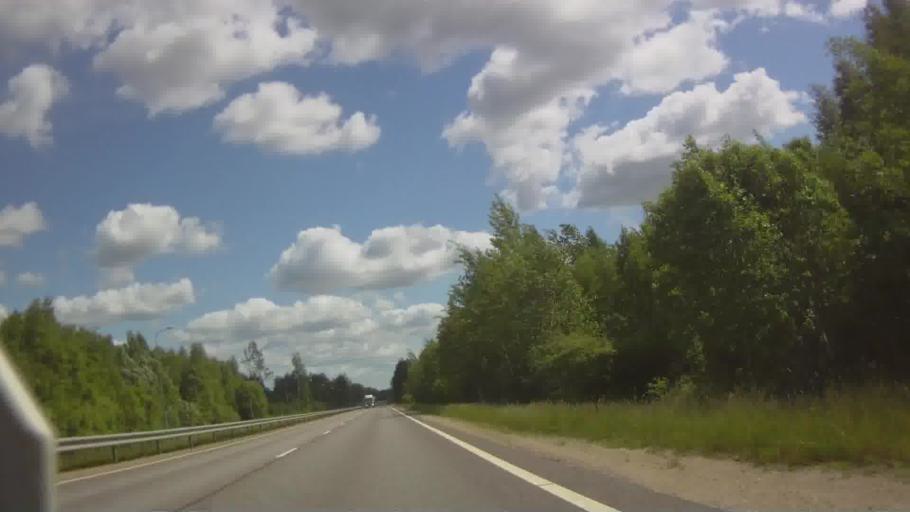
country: LV
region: Livani
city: Livani
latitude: 56.5425
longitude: 26.0833
